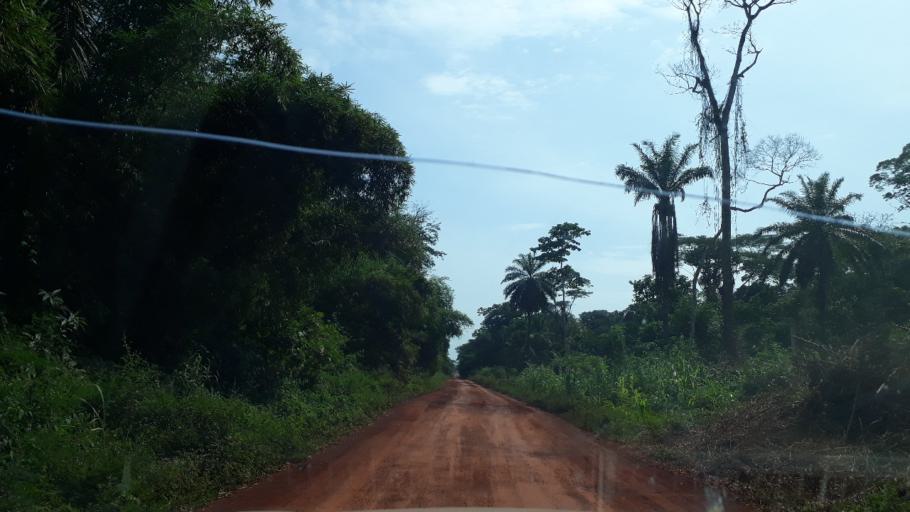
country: CD
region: Eastern Province
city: Wamba
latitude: 1.4000
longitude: 28.0575
